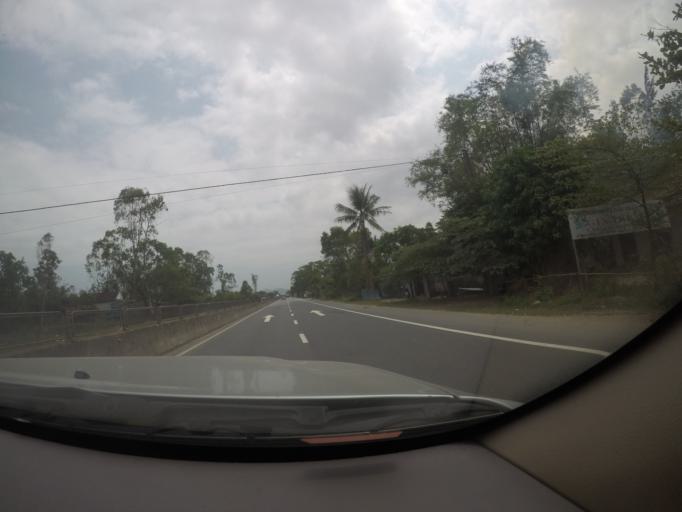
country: VN
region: Thua Thien-Hue
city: Phu Loc
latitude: 16.2724
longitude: 107.9501
